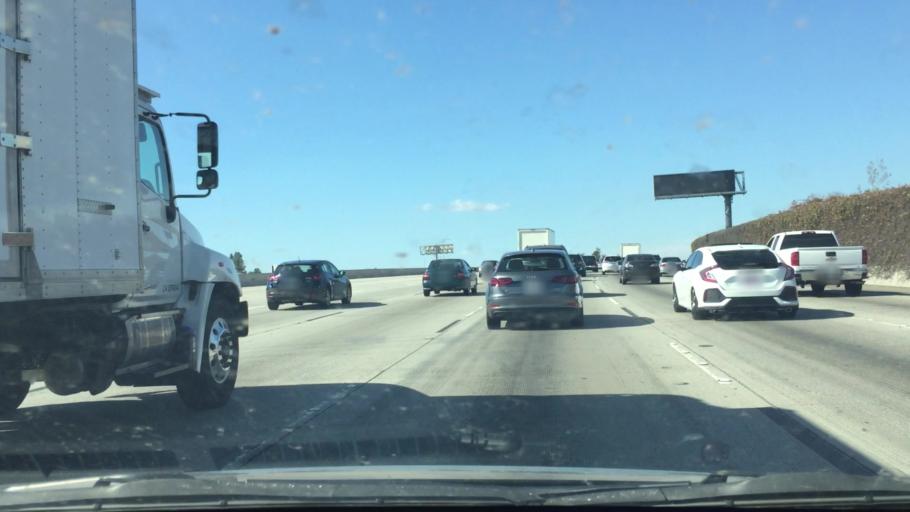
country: US
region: California
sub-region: Orange County
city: Santa Ana
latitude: 33.7586
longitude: -117.8598
